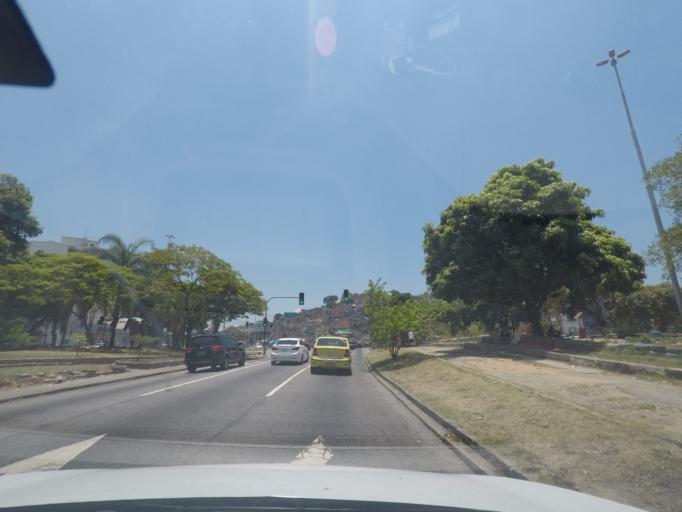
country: BR
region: Rio de Janeiro
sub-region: Rio De Janeiro
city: Rio de Janeiro
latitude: -22.9096
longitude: -43.2383
